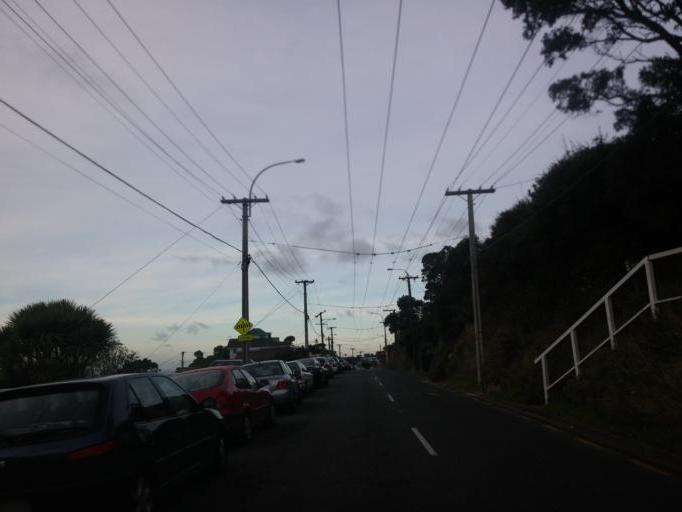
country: NZ
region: Wellington
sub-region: Wellington City
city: Brooklyn
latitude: -41.3143
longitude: 174.7656
